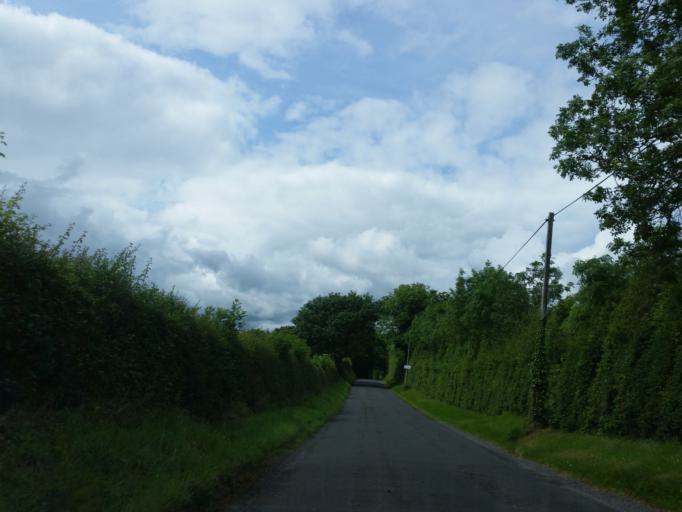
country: IE
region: Ulster
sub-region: County Monaghan
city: Clones
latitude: 54.2131
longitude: -7.2517
